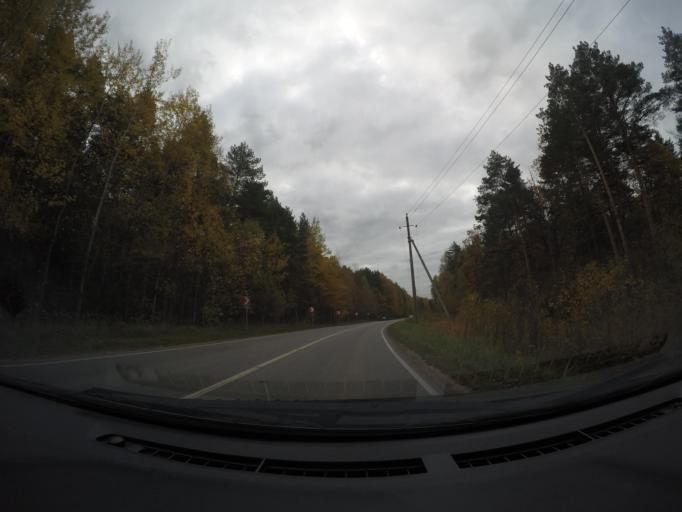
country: RU
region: Moskovskaya
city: Gzhel'
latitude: 55.6374
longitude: 38.4185
